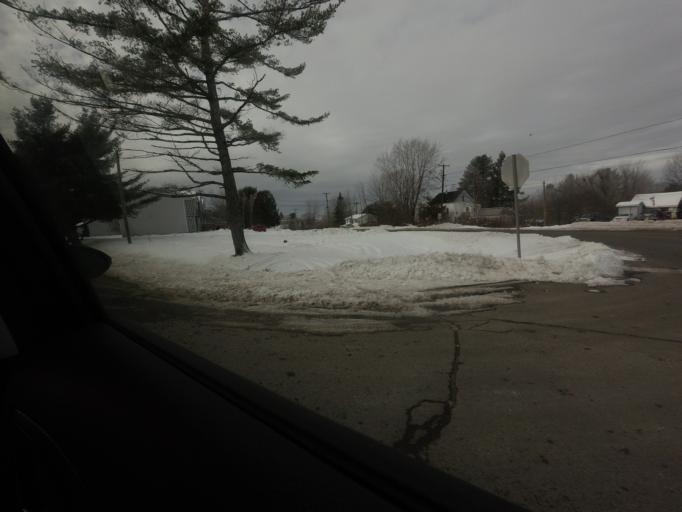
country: CA
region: New Brunswick
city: Oromocto
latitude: 45.8519
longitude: -66.4643
